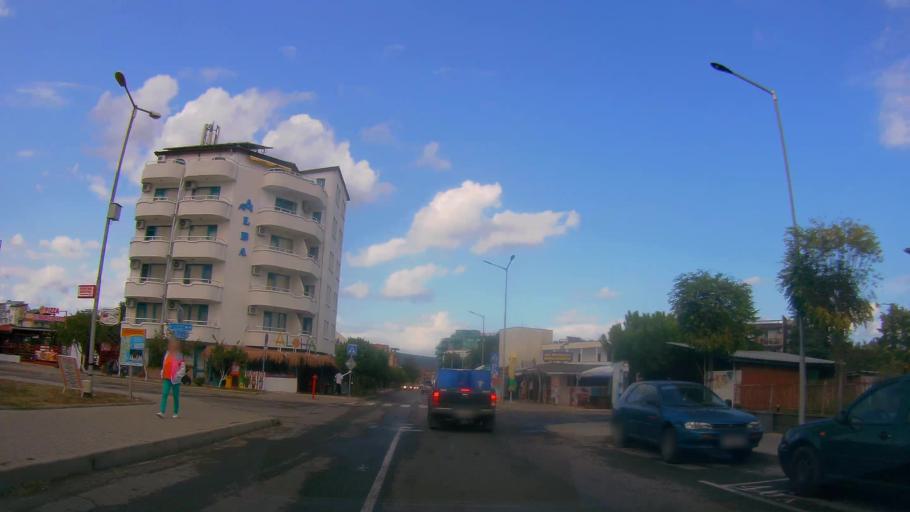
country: BG
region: Burgas
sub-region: Obshtina Primorsko
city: Primorsko
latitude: 42.2704
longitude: 27.7504
